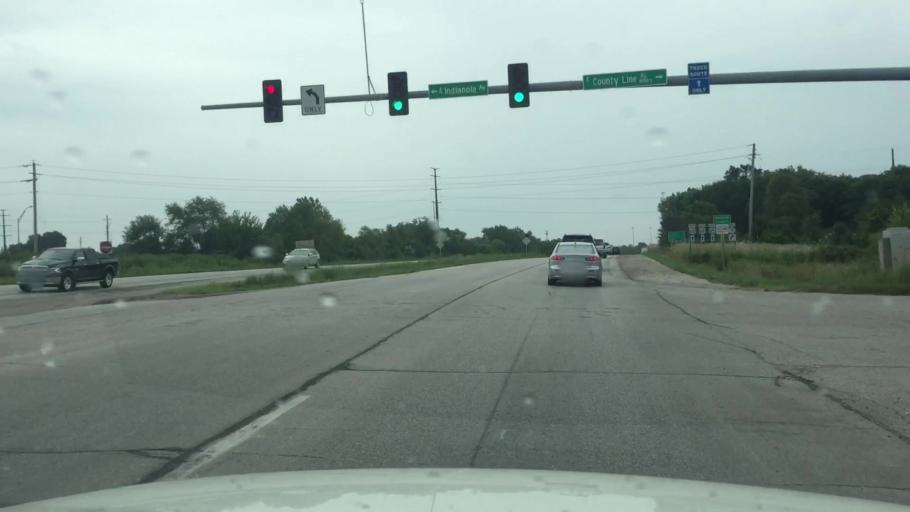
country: US
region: Iowa
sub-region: Warren County
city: Carlisle
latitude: 41.5124
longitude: -93.5788
